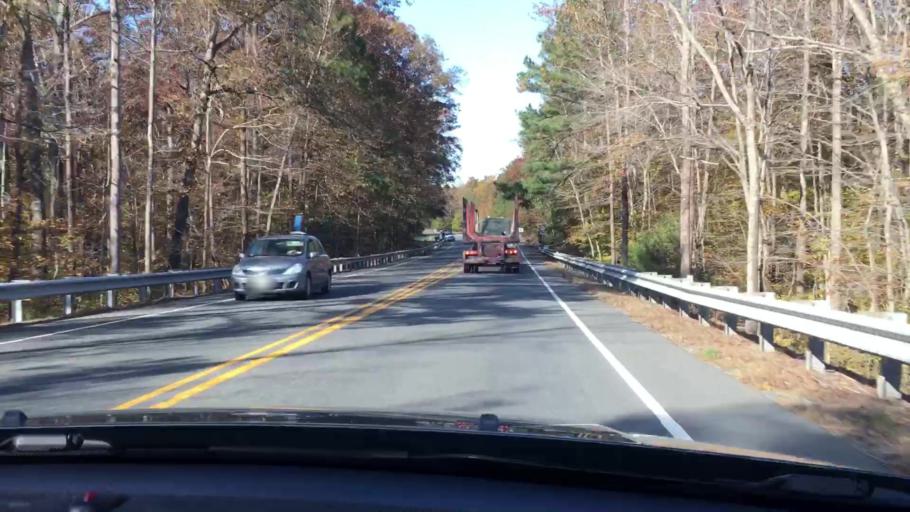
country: US
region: Virginia
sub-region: King William County
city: Central Garage
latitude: 37.7549
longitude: -77.1427
